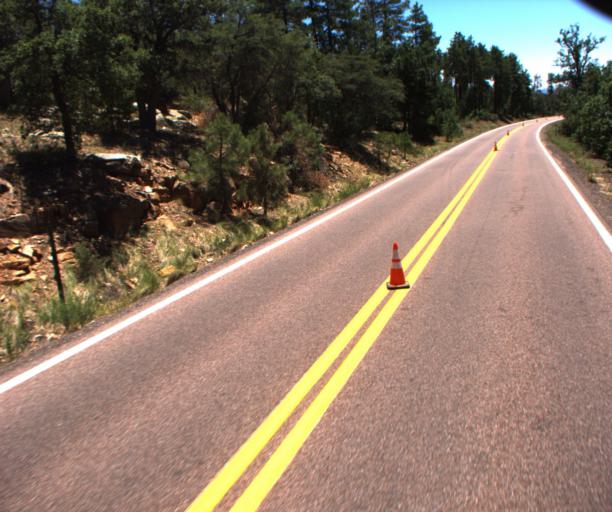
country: US
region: Arizona
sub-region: Gila County
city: Pine
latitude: 34.4288
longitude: -111.5096
